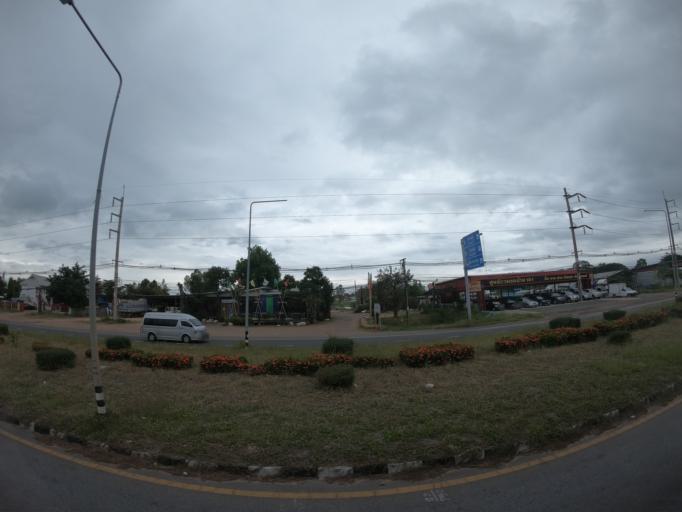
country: TH
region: Roi Et
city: Roi Et
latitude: 16.0434
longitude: 103.6307
